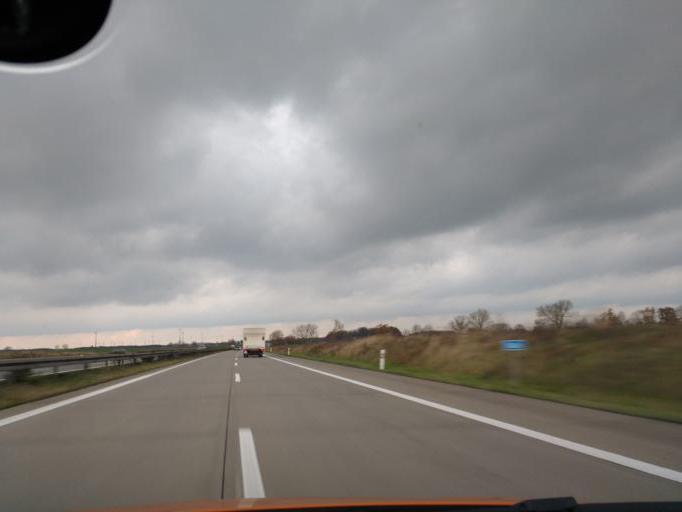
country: DE
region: Brandenburg
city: Heiligengrabe
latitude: 53.1873
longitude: 12.2877
